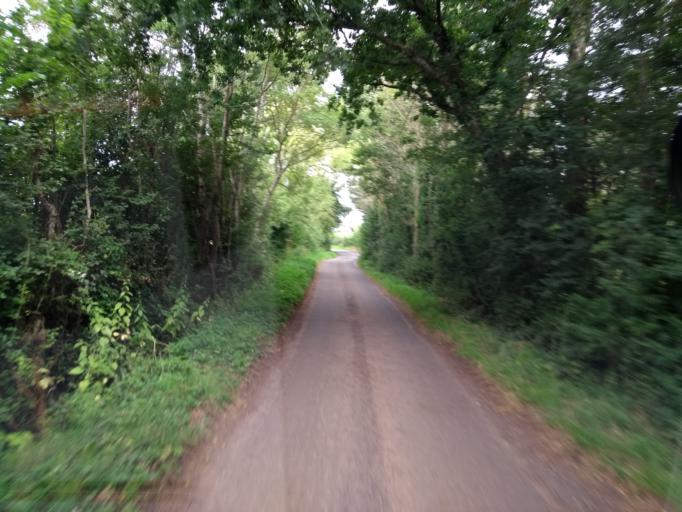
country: GB
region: England
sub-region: Somerset
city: Creech Saint Michael
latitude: 51.0373
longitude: -3.0152
